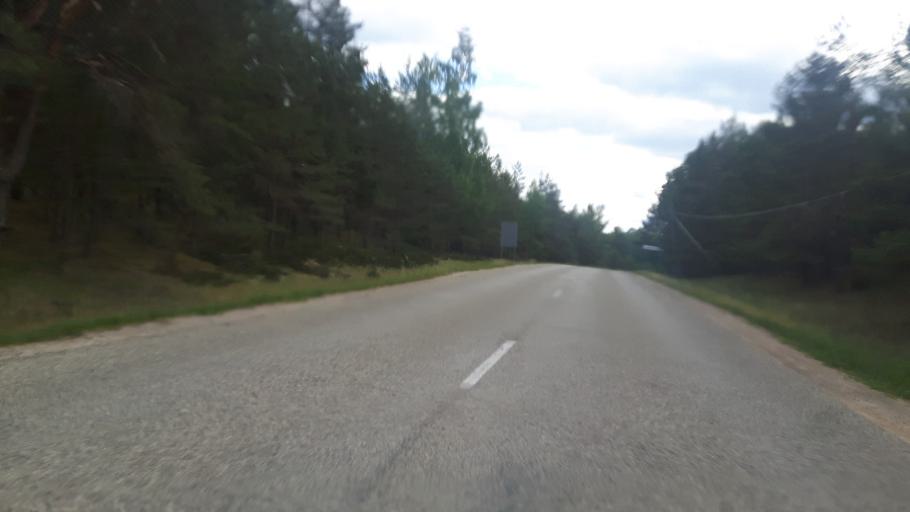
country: LV
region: Engure
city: Smarde
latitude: 57.0393
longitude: 23.3768
